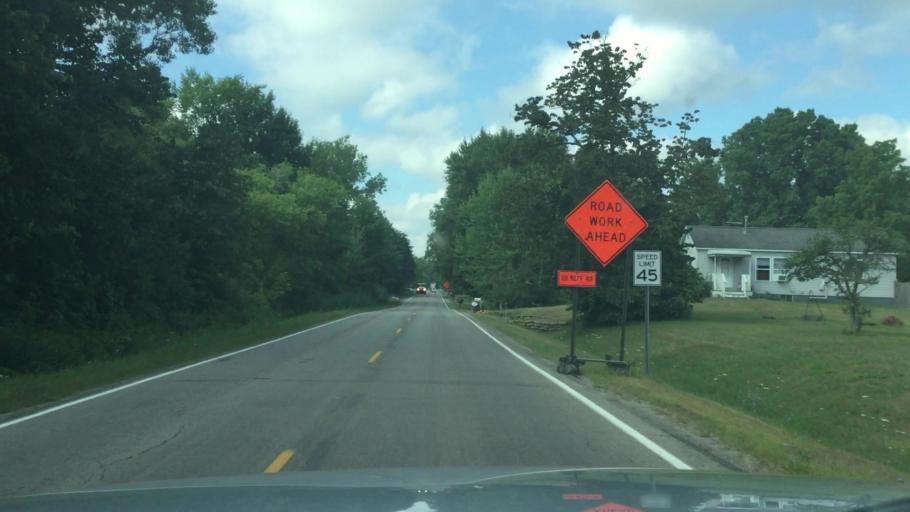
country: US
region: Michigan
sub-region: Genesee County
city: Clio
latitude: 43.2065
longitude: -83.7121
